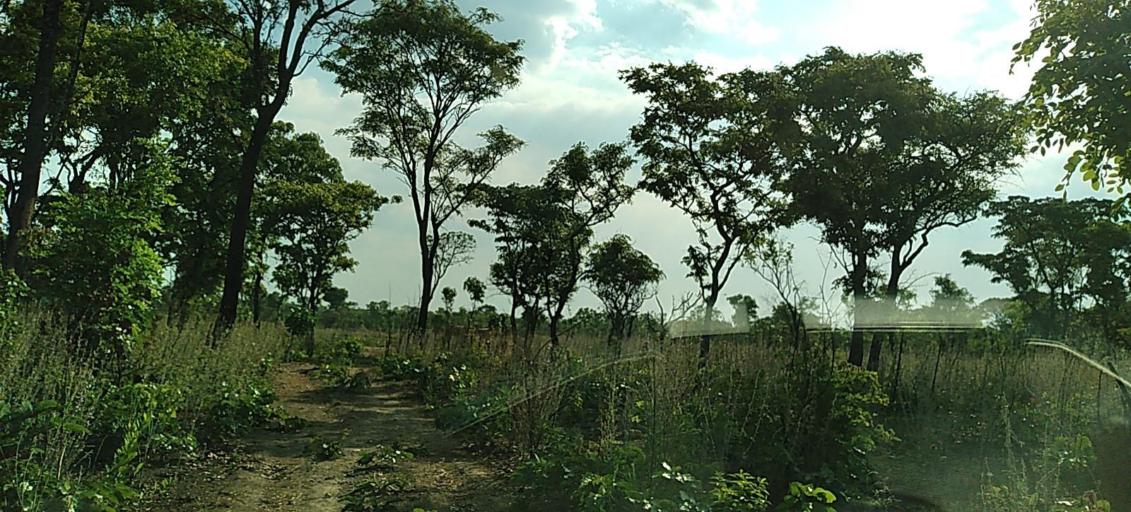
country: ZM
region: Copperbelt
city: Chililabombwe
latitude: -12.3610
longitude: 27.3913
